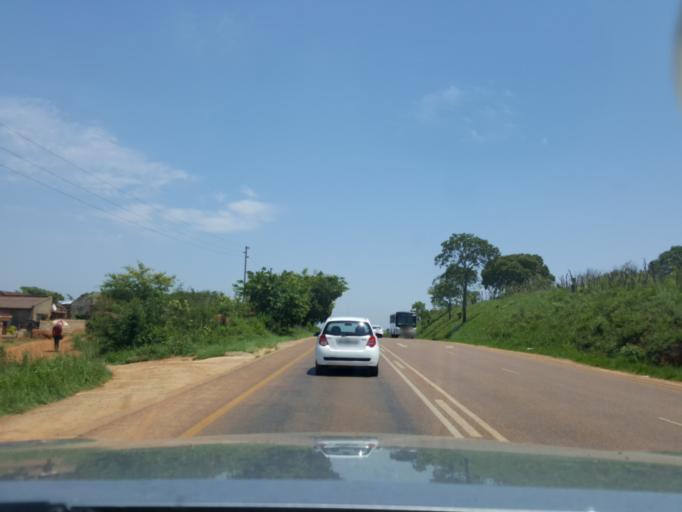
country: ZA
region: Limpopo
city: Thulamahashi
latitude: -24.9164
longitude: 31.1200
